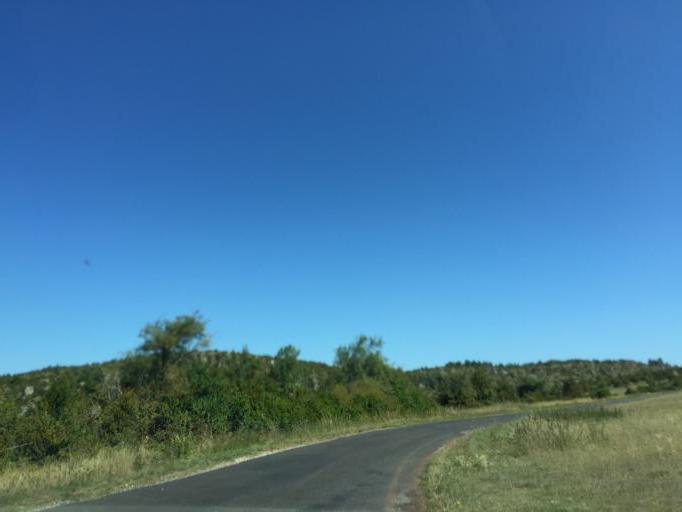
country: FR
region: Midi-Pyrenees
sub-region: Departement de l'Aveyron
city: La Cavalerie
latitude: 43.9010
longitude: 3.2815
